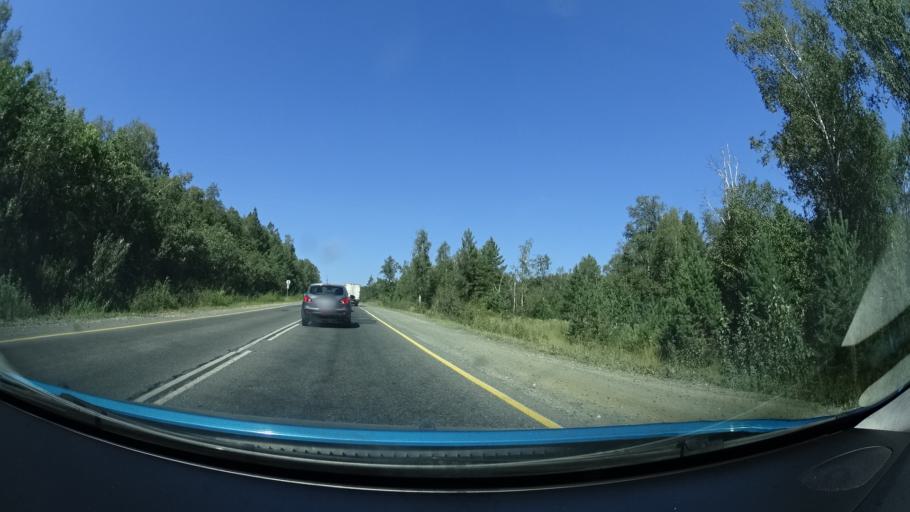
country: RU
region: Bashkortostan
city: Abzakovo
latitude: 53.8902
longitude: 58.5215
